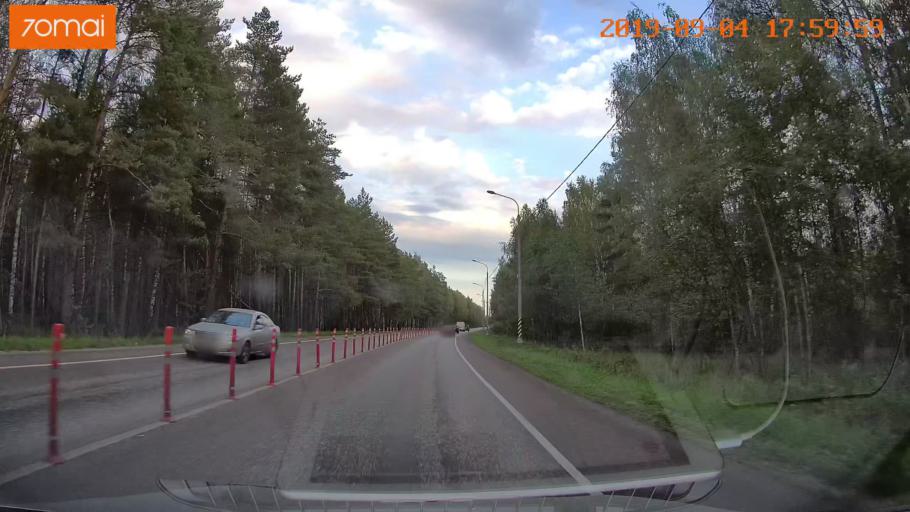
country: RU
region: Moskovskaya
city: Il'inskiy Pogost
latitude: 55.4920
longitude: 38.8529
